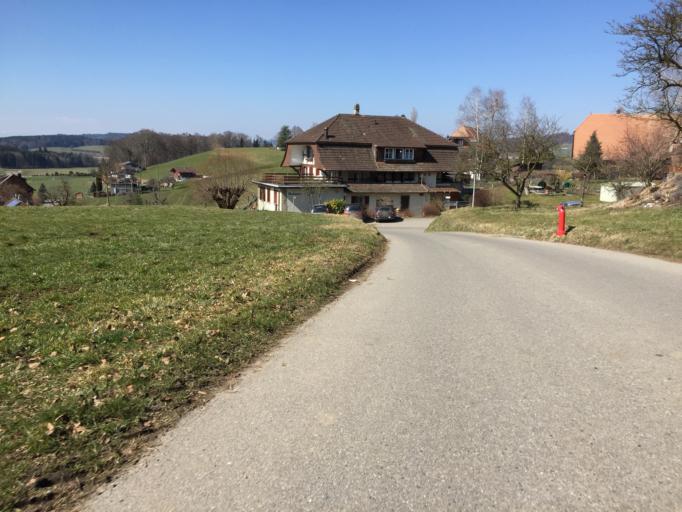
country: CH
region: Bern
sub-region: Bern-Mittelland District
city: Taegertschi
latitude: 46.9053
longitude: 7.5839
